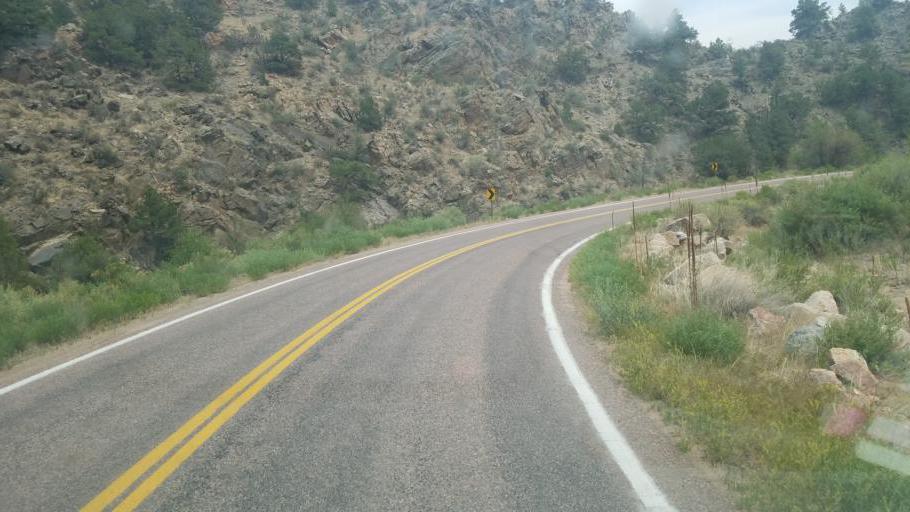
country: US
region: Colorado
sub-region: Fremont County
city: Canon City
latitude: 38.4334
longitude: -105.3927
